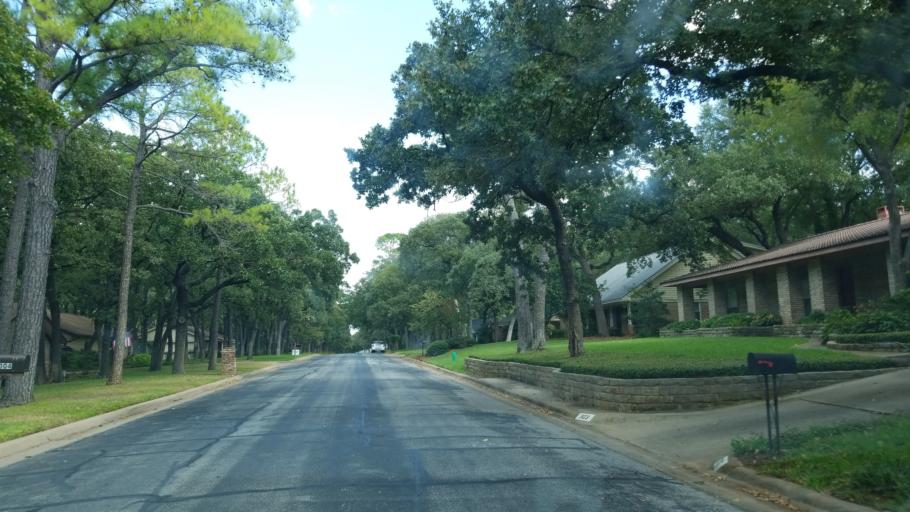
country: US
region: Texas
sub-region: Tarrant County
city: Euless
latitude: 32.8631
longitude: -97.0867
